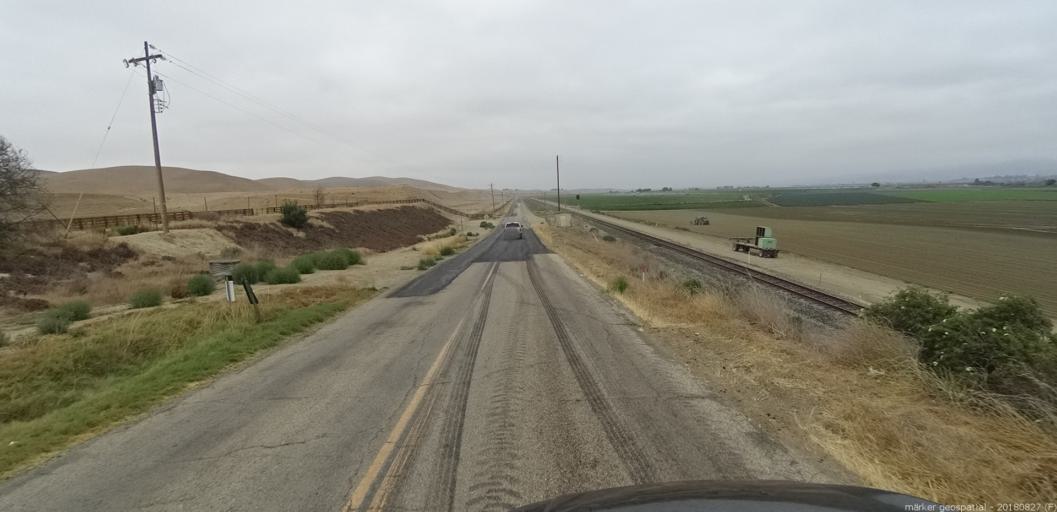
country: US
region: California
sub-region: Monterey County
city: Greenfield
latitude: 36.3124
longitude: -121.1696
